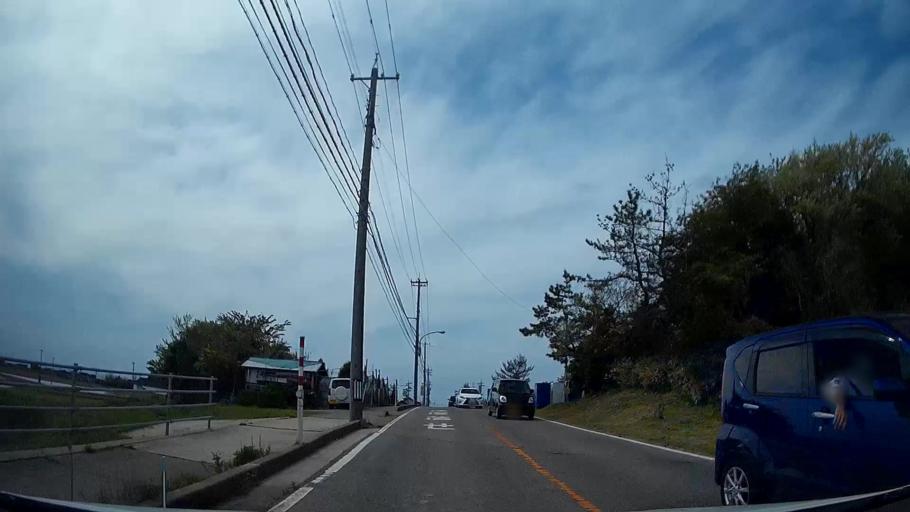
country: JP
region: Ishikawa
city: Hakui
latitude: 37.0161
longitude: 136.7520
